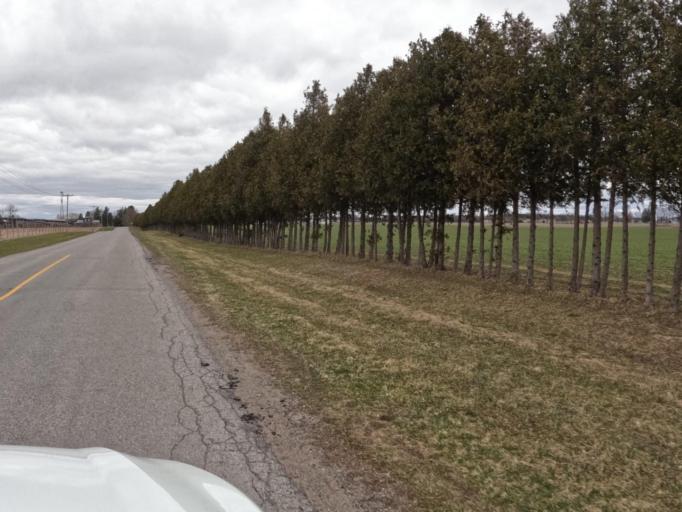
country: CA
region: Ontario
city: Norfolk County
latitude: 42.9579
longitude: -80.3954
